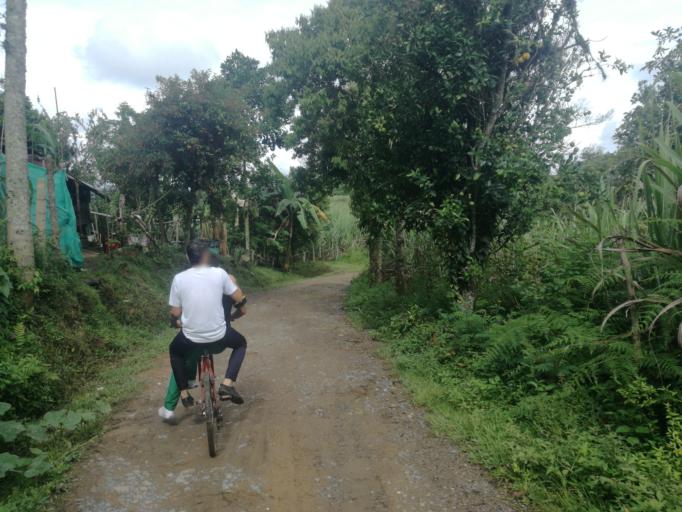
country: CO
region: Boyaca
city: Santana
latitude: 6.0650
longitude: -73.4839
